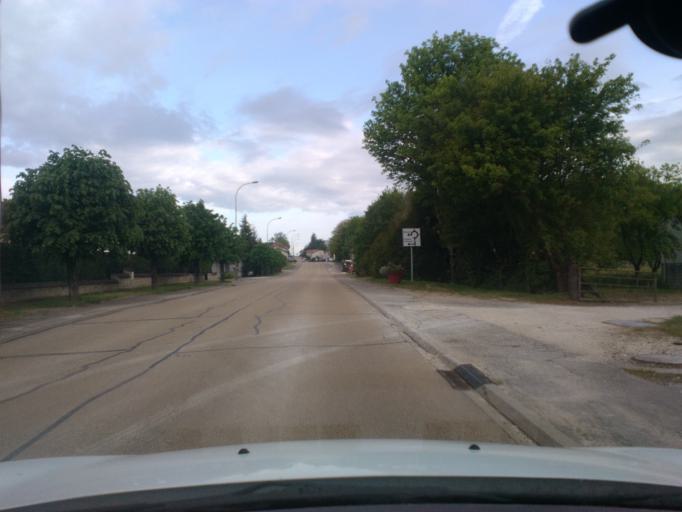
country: FR
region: Champagne-Ardenne
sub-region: Departement de la Haute-Marne
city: Lavilleneuve-au-Roi
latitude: 48.2237
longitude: 4.8920
